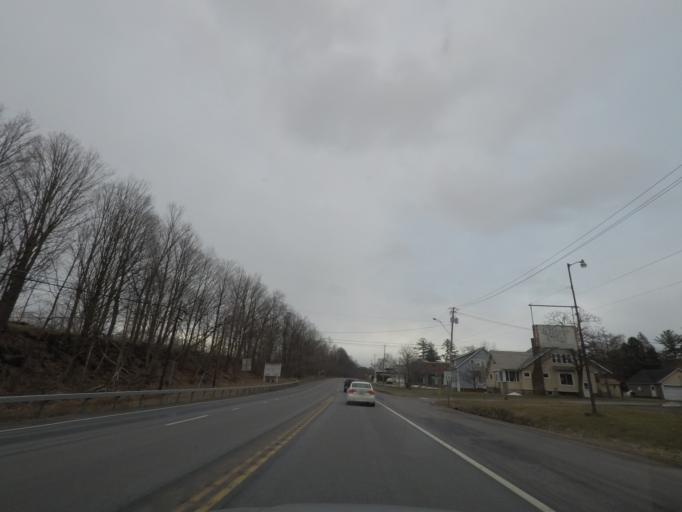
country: US
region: New York
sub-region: Oneida County
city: Sherrill
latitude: 43.0766
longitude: -75.6040
